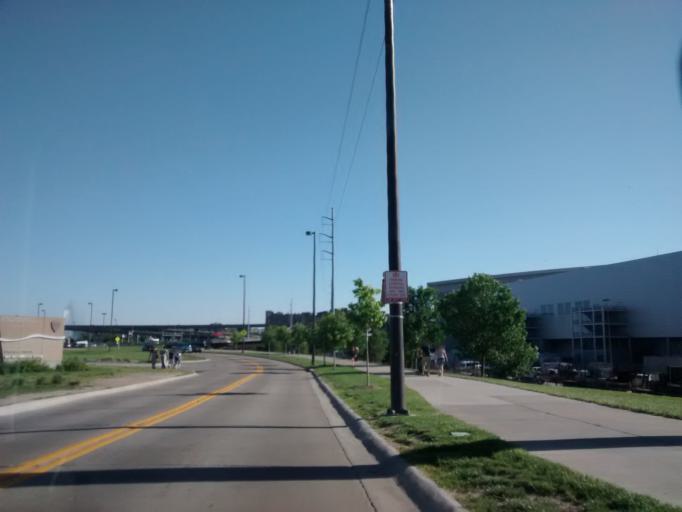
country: US
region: Nebraska
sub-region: Douglas County
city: Omaha
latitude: 41.2652
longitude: -95.9258
